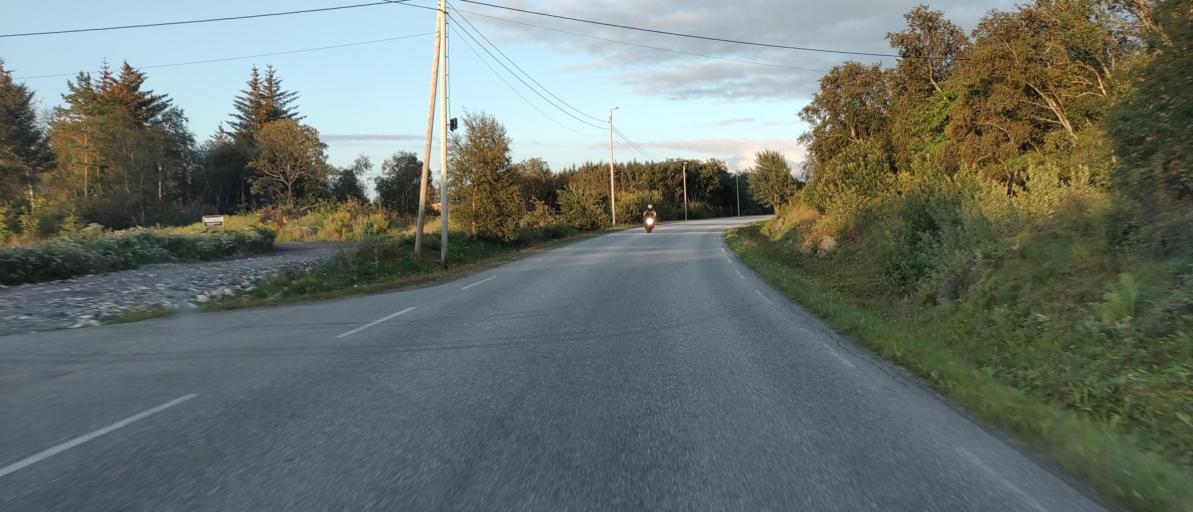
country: NO
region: More og Romsdal
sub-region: Fraena
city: Elnesvagen
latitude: 62.9914
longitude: 7.1909
